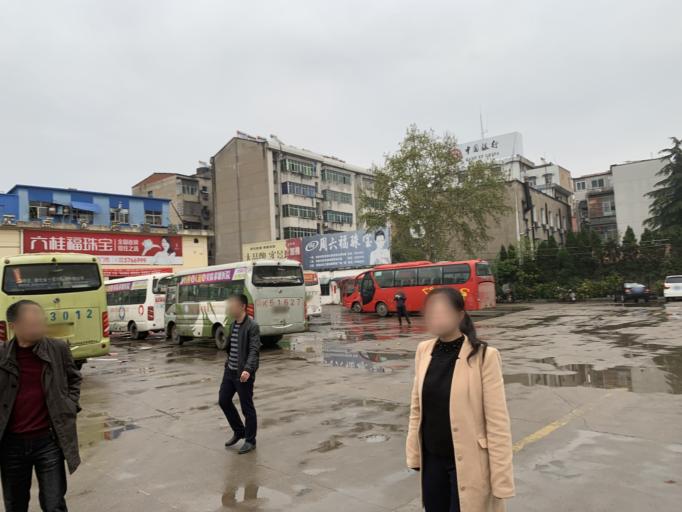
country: CN
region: Hubei
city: Anlu
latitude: 31.2558
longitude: 113.6868
